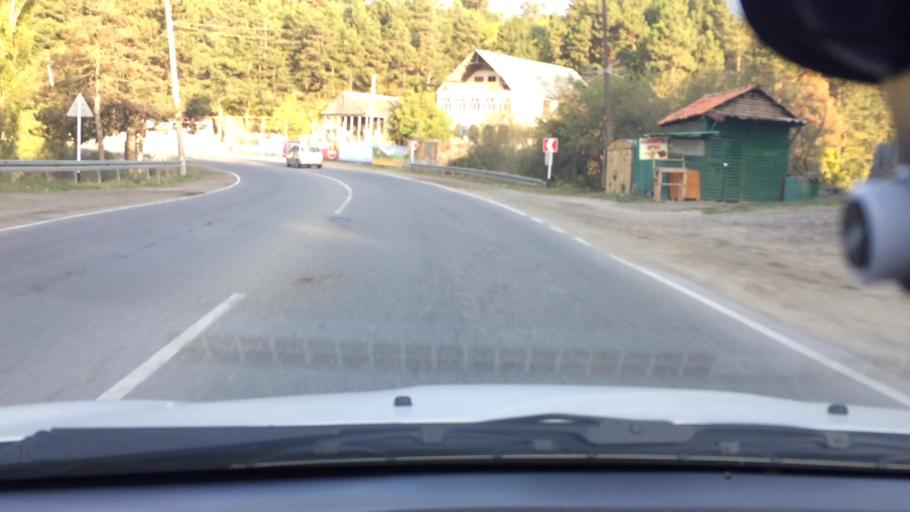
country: GE
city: Surami
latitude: 42.0276
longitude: 43.5599
